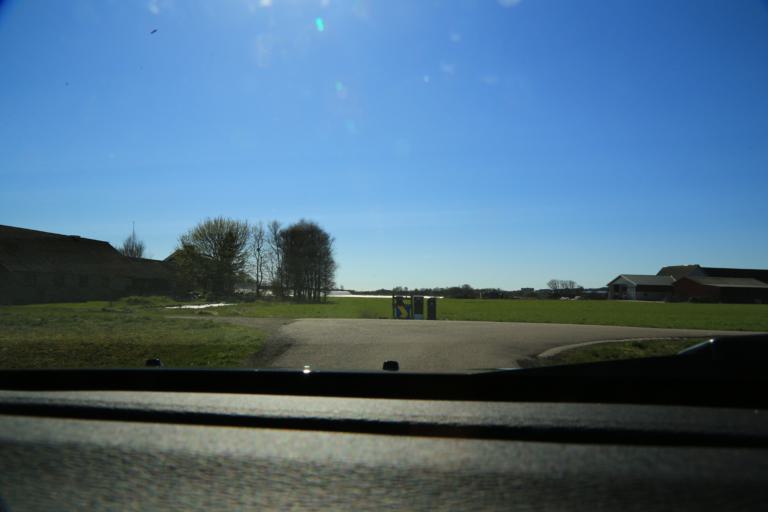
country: SE
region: Halland
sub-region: Varbergs Kommun
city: Traslovslage
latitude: 57.0894
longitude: 12.2983
